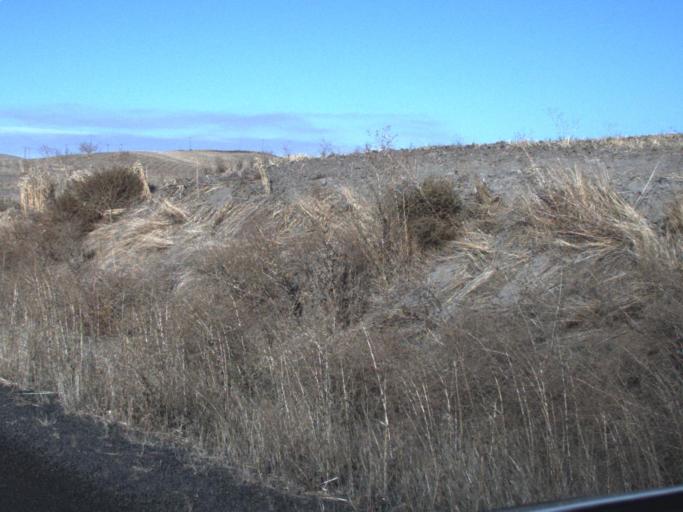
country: US
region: Washington
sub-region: Walla Walla County
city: Walla Walla
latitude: 46.1336
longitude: -118.3760
